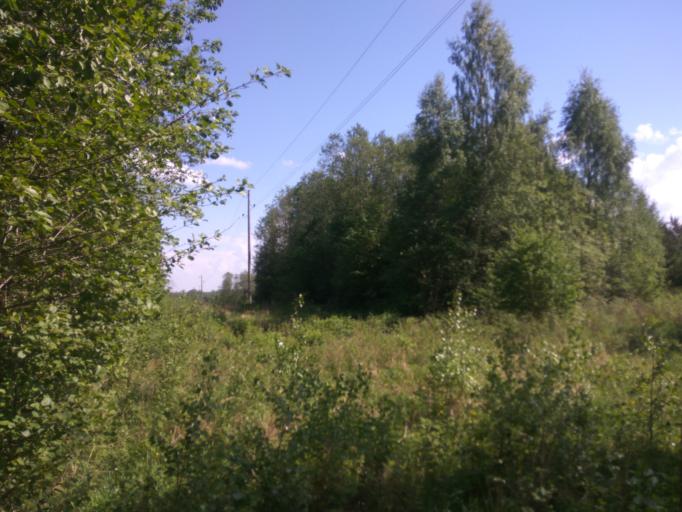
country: LV
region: Kuldigas Rajons
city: Kuldiga
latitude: 57.1749
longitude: 22.0182
